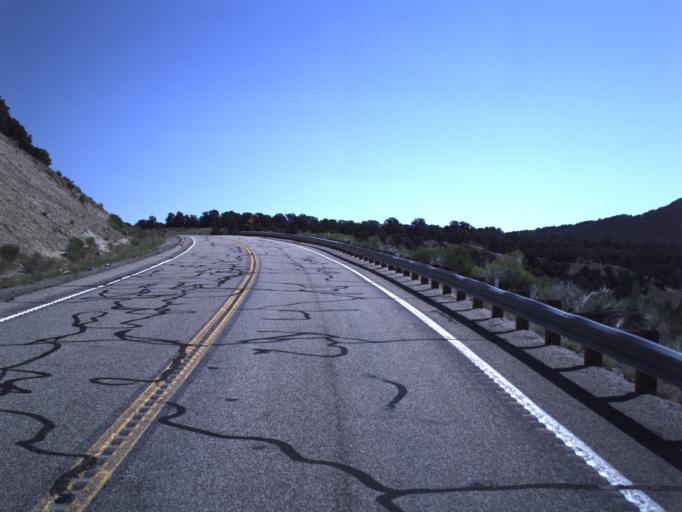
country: US
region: Utah
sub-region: Wayne County
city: Loa
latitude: 38.6909
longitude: -111.3985
